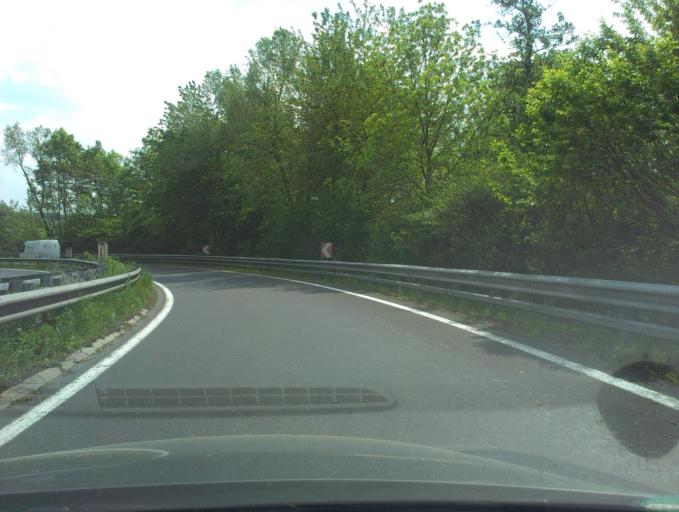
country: AT
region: Upper Austria
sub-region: Politischer Bezirk Vocklabruck
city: Wolfsegg am Hausruck
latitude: 48.1985
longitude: 13.6399
